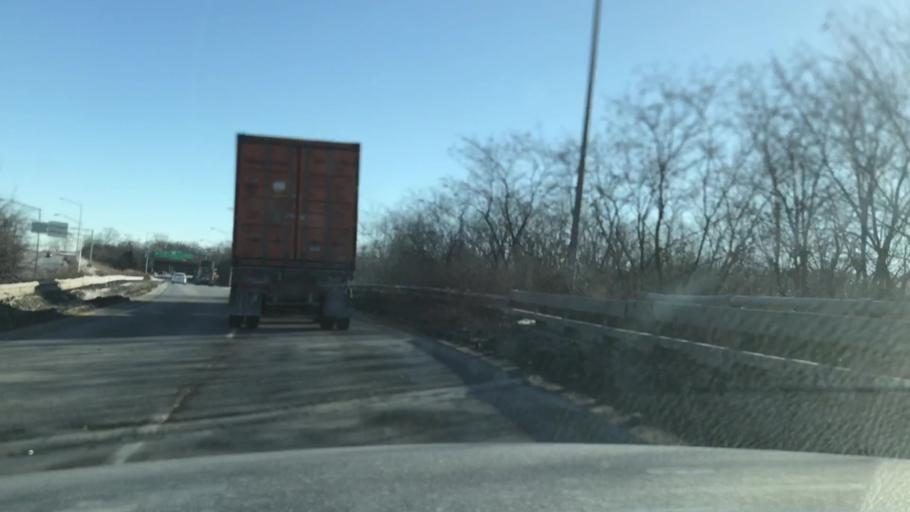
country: US
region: Illinois
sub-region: Cook County
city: Willow Springs
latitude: 41.7453
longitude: -87.8520
